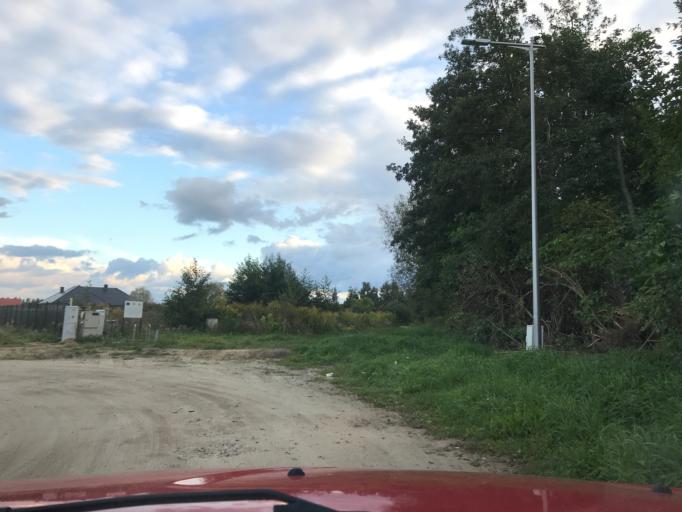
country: PL
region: Greater Poland Voivodeship
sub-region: Powiat poznanski
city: Plewiska
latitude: 52.3981
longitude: 16.7900
